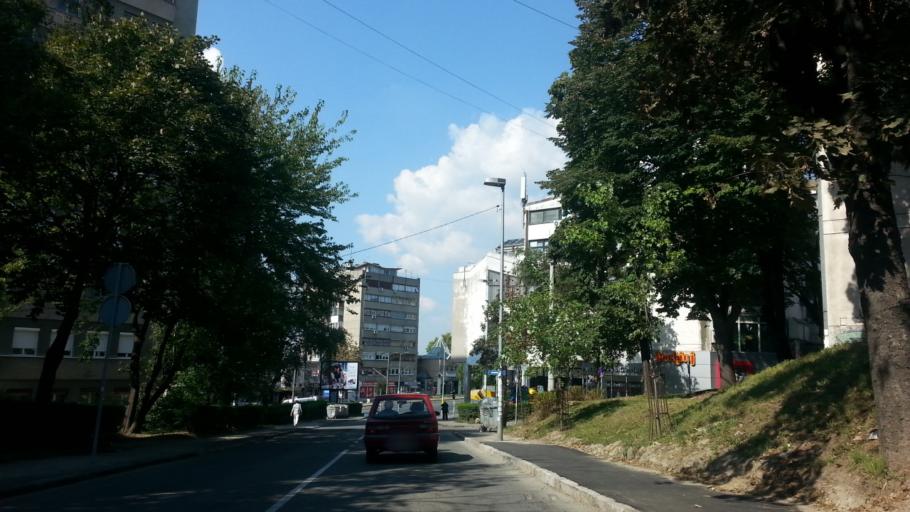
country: RS
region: Central Serbia
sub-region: Belgrade
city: Cukarica
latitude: 44.7734
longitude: 20.4150
